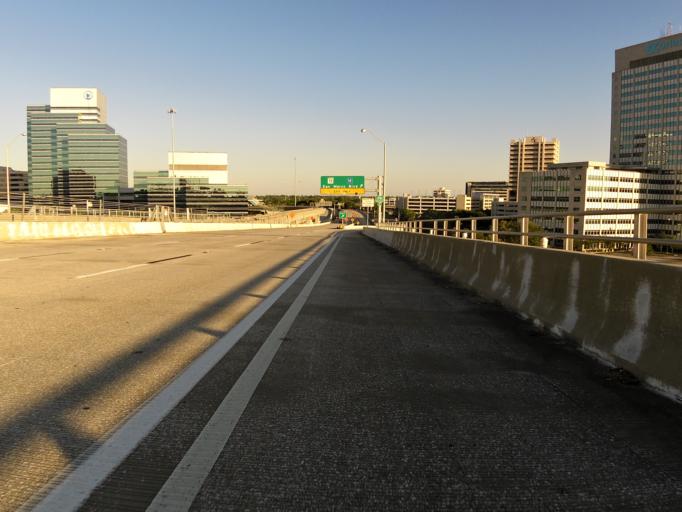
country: US
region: Florida
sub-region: Duval County
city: Jacksonville
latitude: 30.3192
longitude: -81.6634
